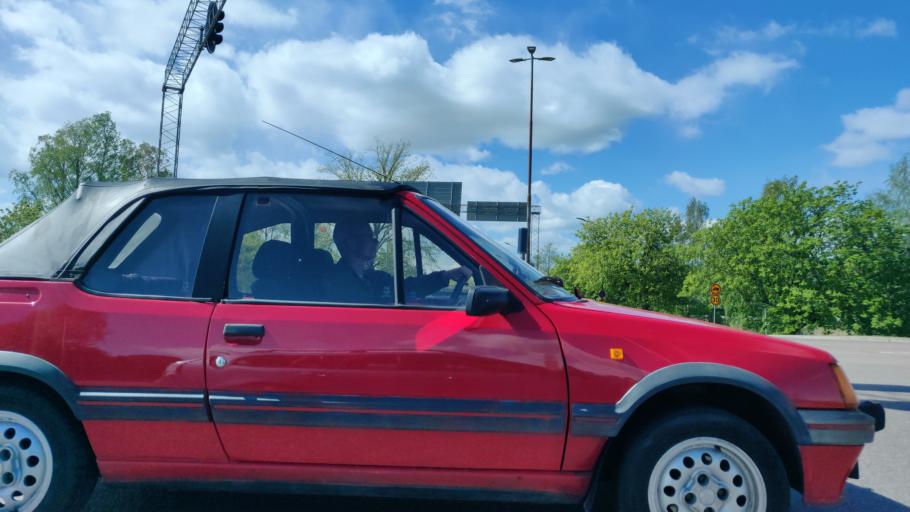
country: SE
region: Vaermland
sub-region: Karlstads Kommun
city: Karlstad
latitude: 59.3799
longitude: 13.4887
